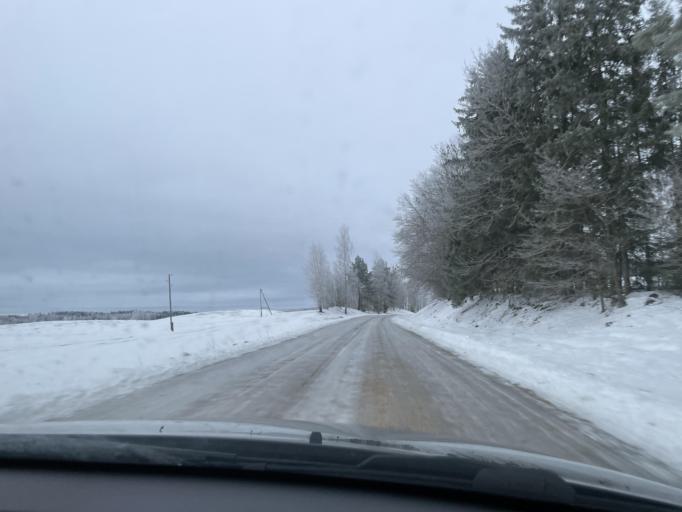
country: LV
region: Ludzas Rajons
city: Ludza
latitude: 56.4532
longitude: 27.5557
